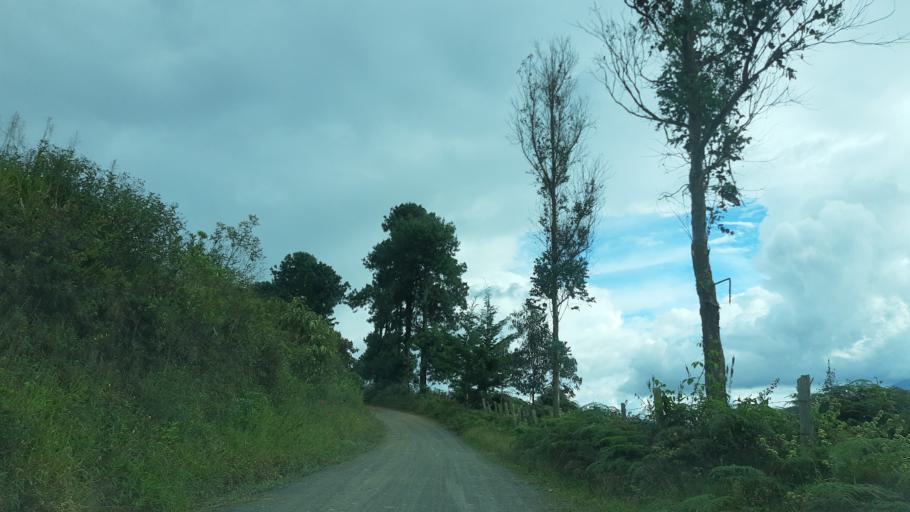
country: CO
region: Boyaca
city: Garagoa
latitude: 5.0012
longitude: -73.3375
